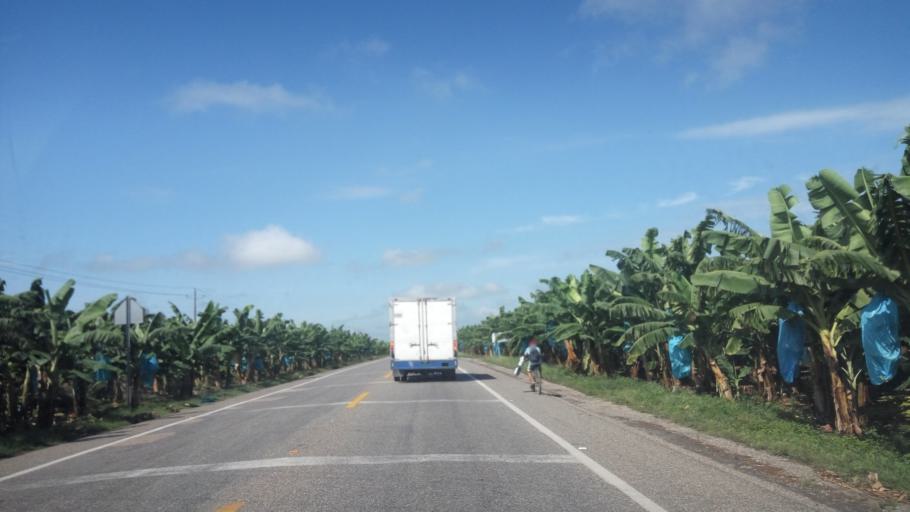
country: MX
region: Tabasco
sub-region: Teapa
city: Eureka y Belen
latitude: 17.6532
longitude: -92.9601
